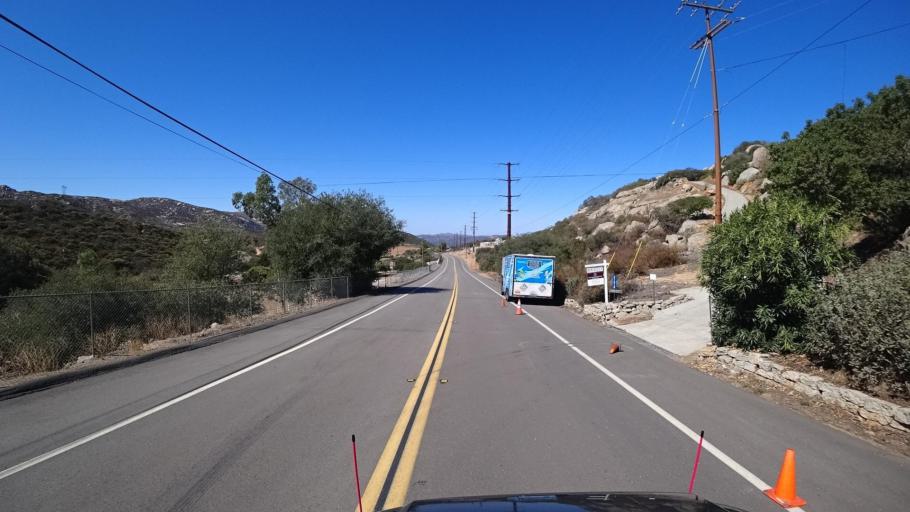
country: US
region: California
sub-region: San Diego County
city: Alpine
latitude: 32.7691
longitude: -116.6966
